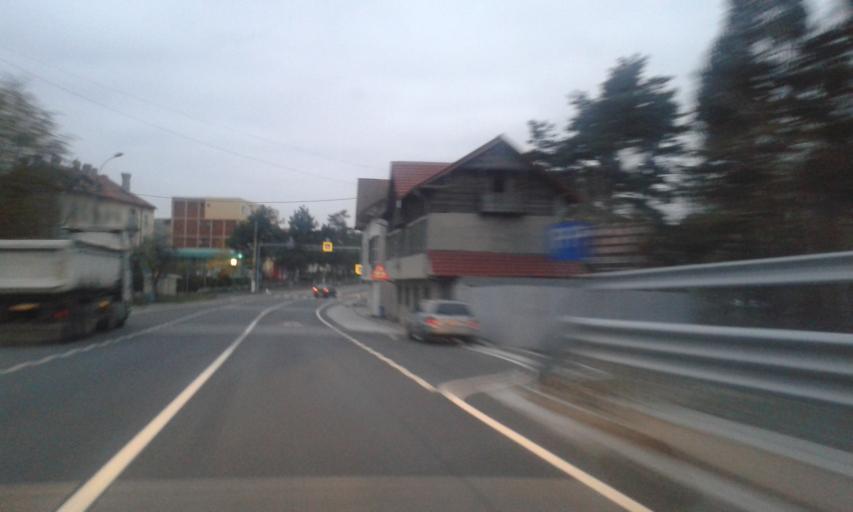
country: RO
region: Gorj
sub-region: Comuna Bumbesti-Jiu
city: Bumbesti-Jiu
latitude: 45.1815
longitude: 23.3790
